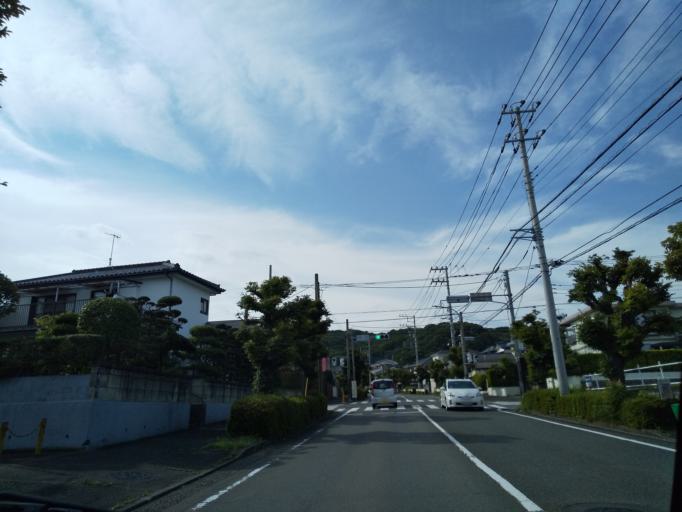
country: JP
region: Kanagawa
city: Zama
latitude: 35.4903
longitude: 139.3352
